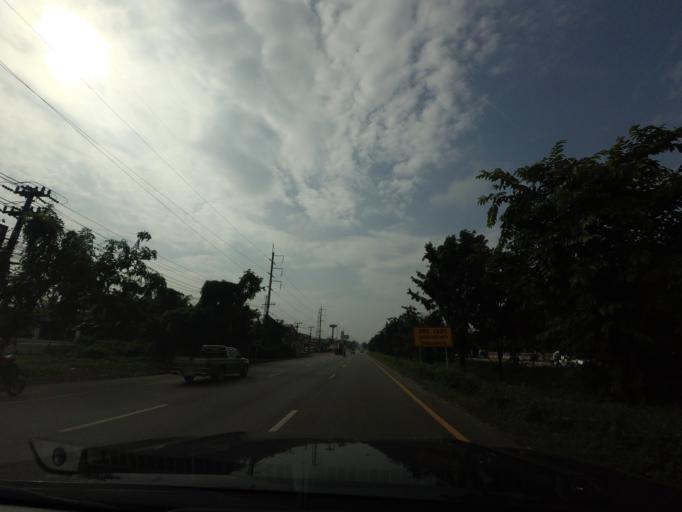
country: TH
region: Nong Khai
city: Nong Khai
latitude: 17.8399
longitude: 102.7534
